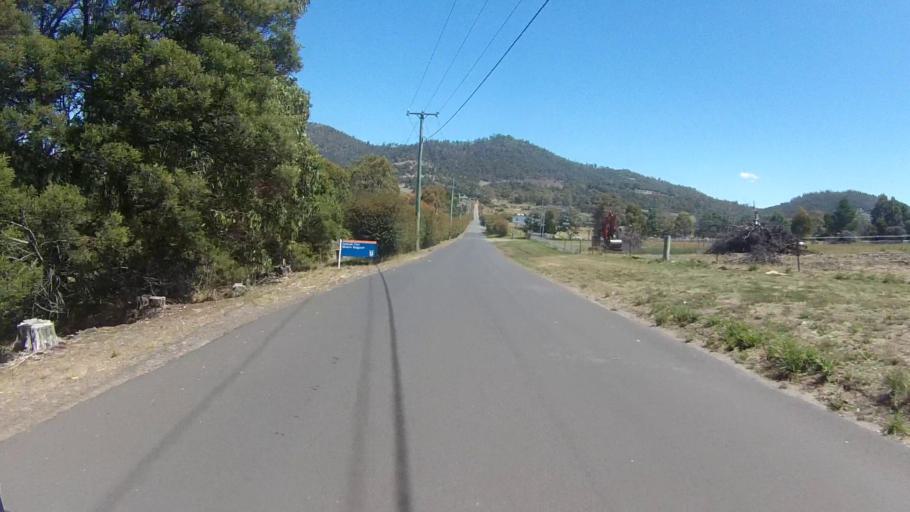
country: AU
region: Tasmania
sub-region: Clarence
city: Cambridge
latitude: -42.8412
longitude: 147.4618
